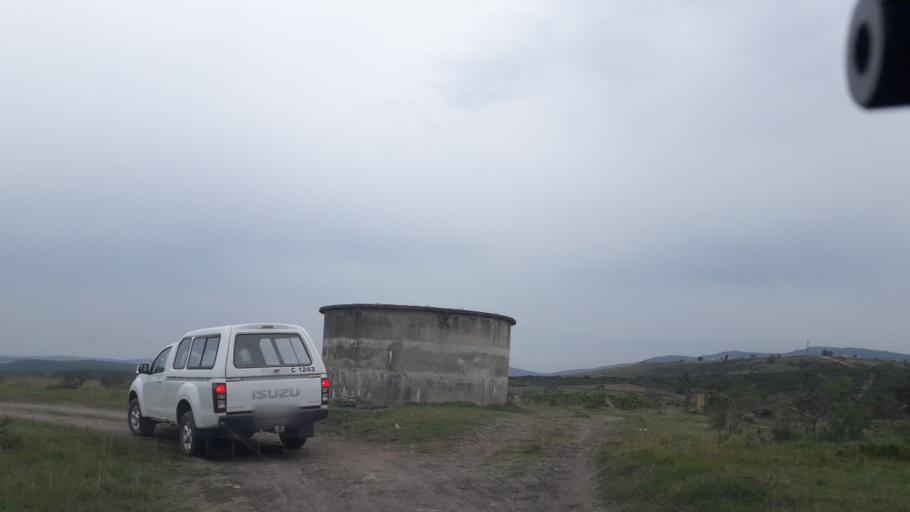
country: ZA
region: Eastern Cape
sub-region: Buffalo City Metropolitan Municipality
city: Bhisho
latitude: -32.7956
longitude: 27.3389
